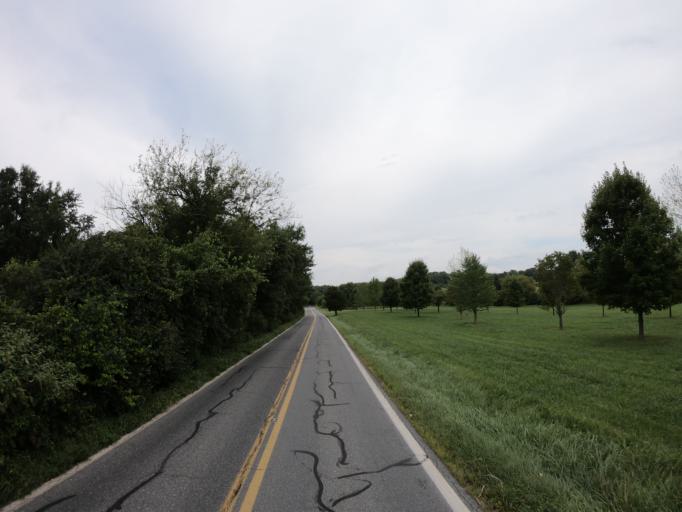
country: US
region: Maryland
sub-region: Montgomery County
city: Olney
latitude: 39.2171
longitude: -77.1079
